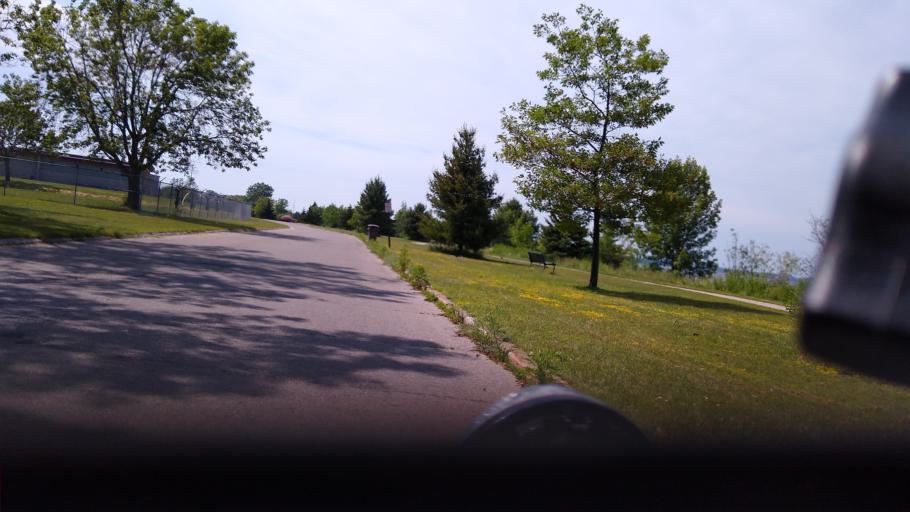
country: US
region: Michigan
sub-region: Delta County
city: Escanaba
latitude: 45.7439
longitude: -87.0388
